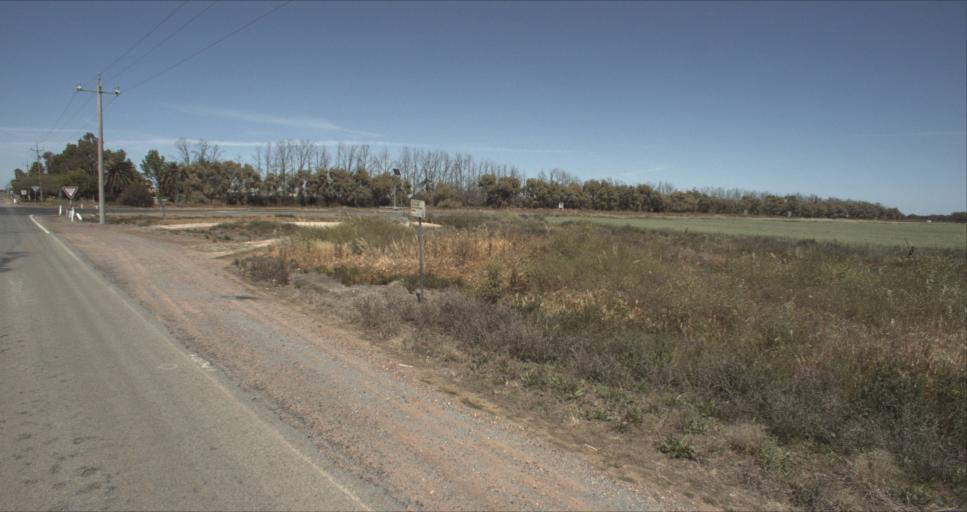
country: AU
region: New South Wales
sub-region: Leeton
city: Leeton
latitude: -34.5191
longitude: 146.2836
